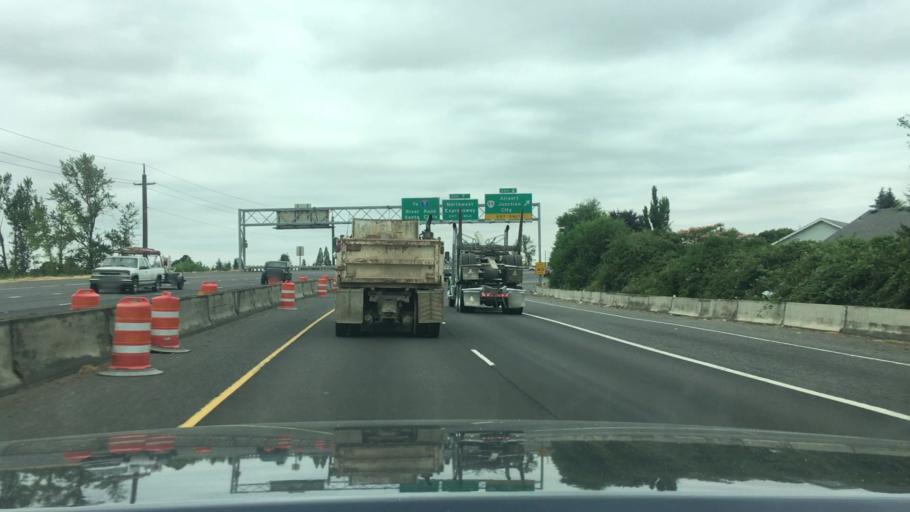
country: US
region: Oregon
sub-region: Lane County
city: Eugene
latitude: 44.0925
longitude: -123.1708
